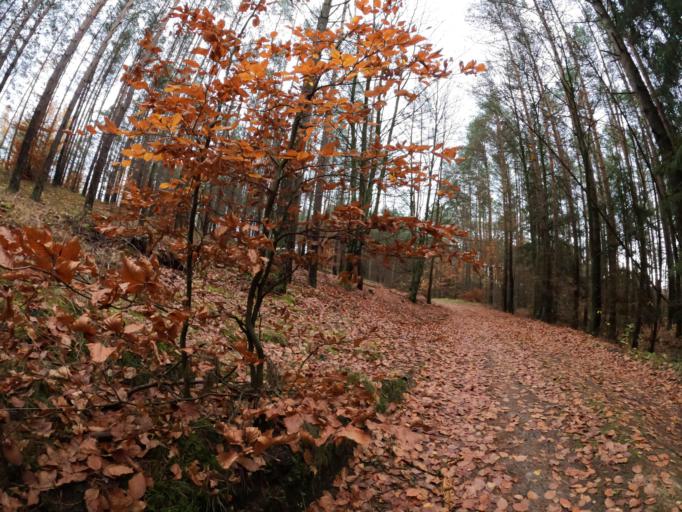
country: PL
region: West Pomeranian Voivodeship
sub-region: Powiat walecki
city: Miroslawiec
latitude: 53.3217
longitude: 16.1126
